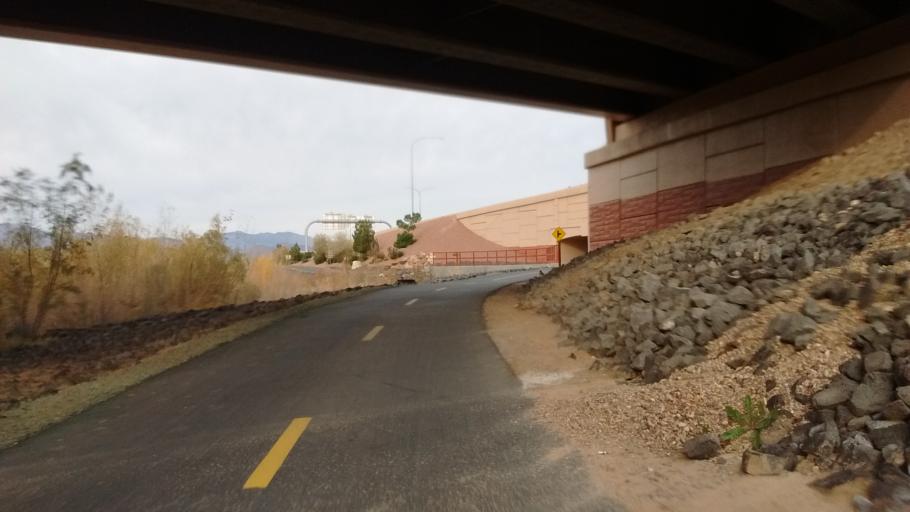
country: US
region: Utah
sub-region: Washington County
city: Saint George
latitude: 37.0746
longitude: -113.5851
